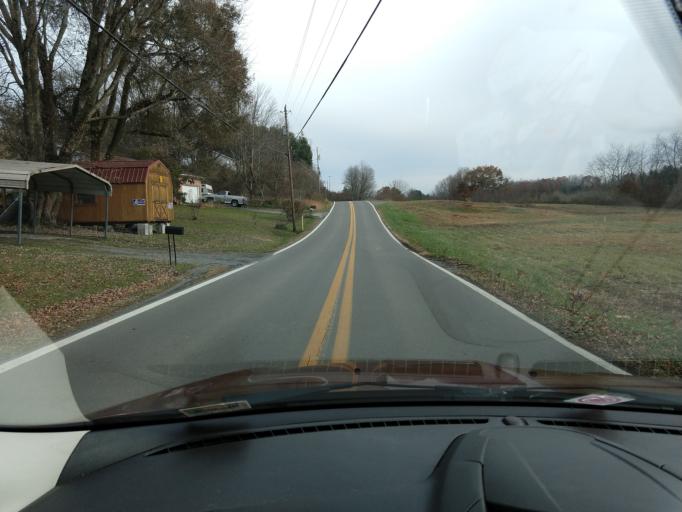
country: US
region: West Virginia
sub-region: Nicholas County
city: Summersville
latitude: 38.2933
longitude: -80.8364
